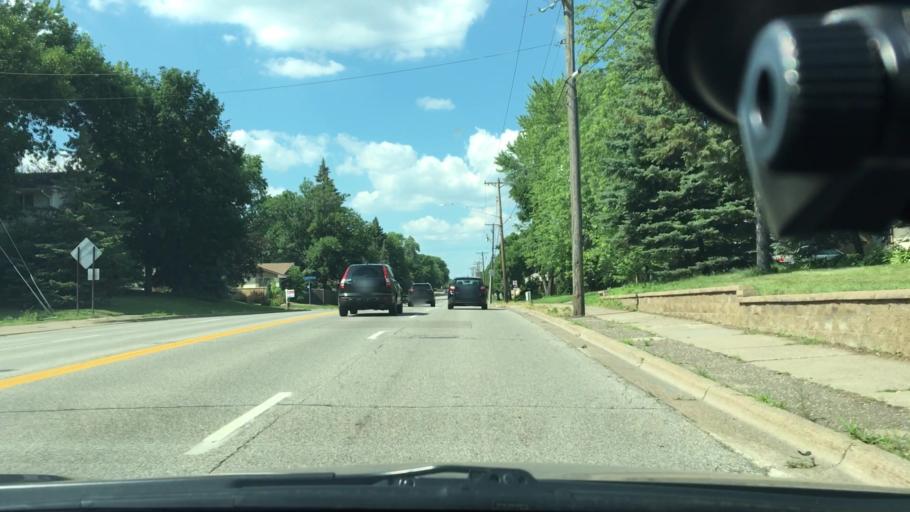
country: US
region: Minnesota
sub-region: Hennepin County
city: New Hope
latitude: 45.0099
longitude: -93.3803
